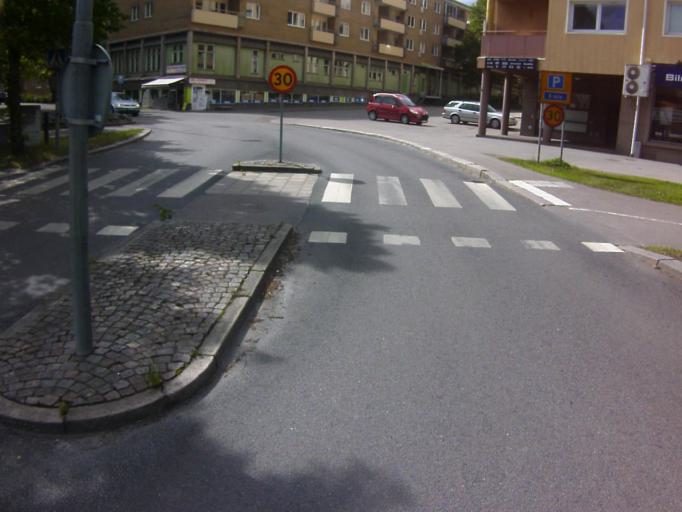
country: SE
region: Soedermanland
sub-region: Eskilstuna Kommun
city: Eskilstuna
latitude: 59.3708
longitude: 16.4990
